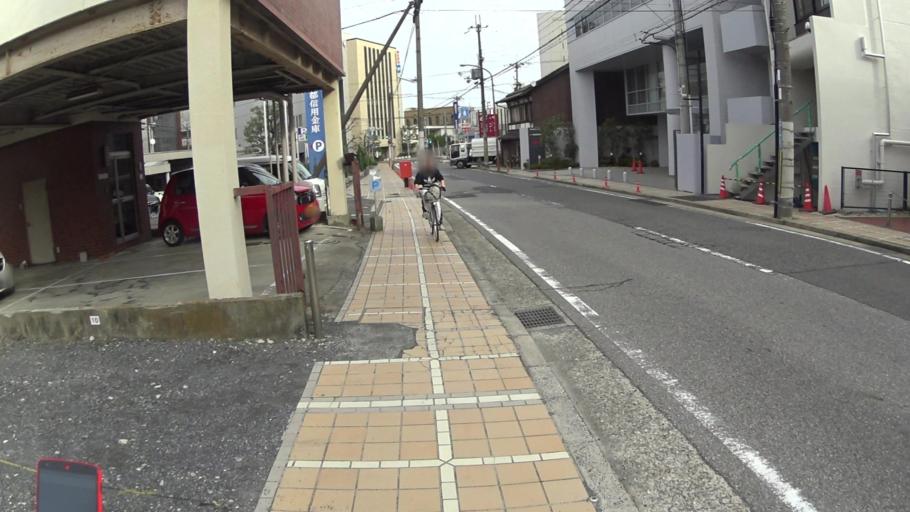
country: JP
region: Shiga Prefecture
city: Otsu-shi
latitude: 35.0091
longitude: 135.8650
